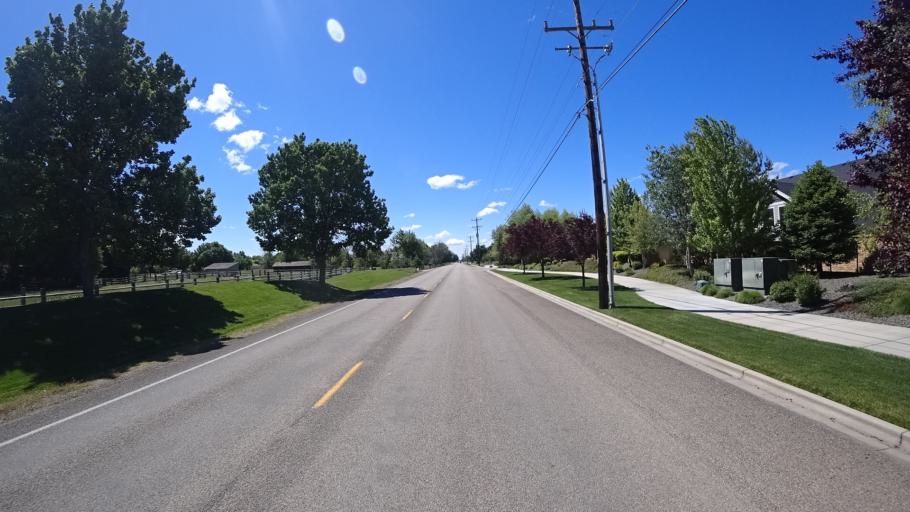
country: US
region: Idaho
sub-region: Ada County
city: Eagle
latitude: 43.6571
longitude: -116.3745
